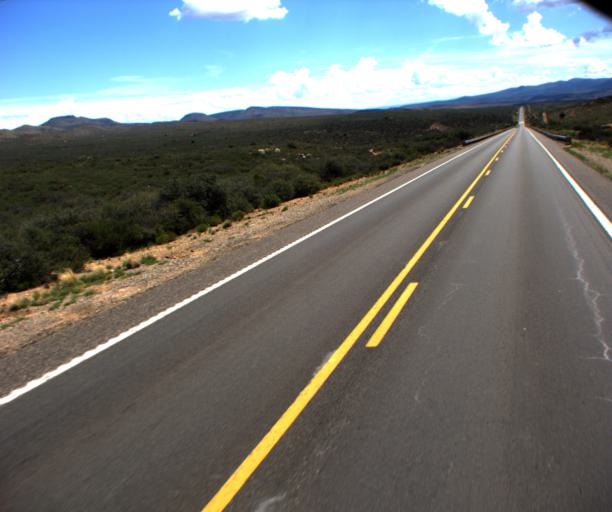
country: US
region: Arizona
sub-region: Yavapai County
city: Dewey-Humboldt
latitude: 34.5332
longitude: -112.1280
